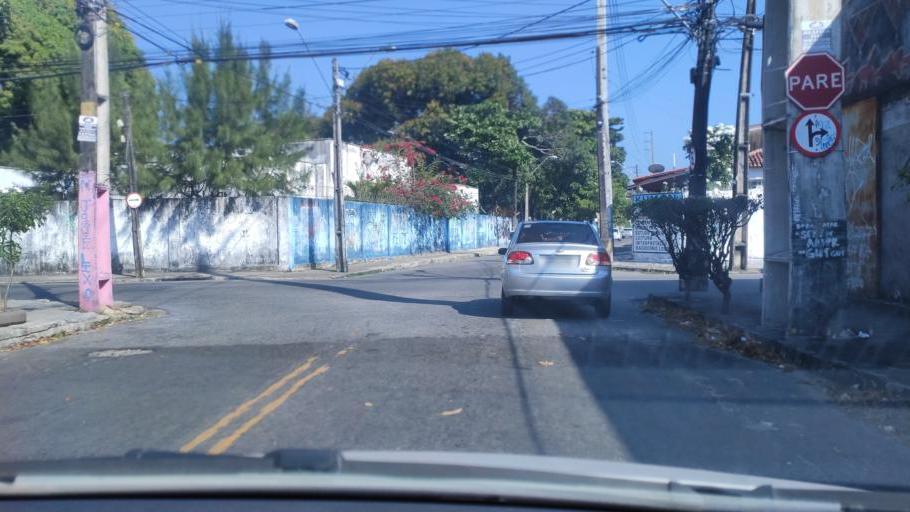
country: BR
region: Ceara
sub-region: Fortaleza
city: Fortaleza
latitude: -3.7418
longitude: -38.5358
